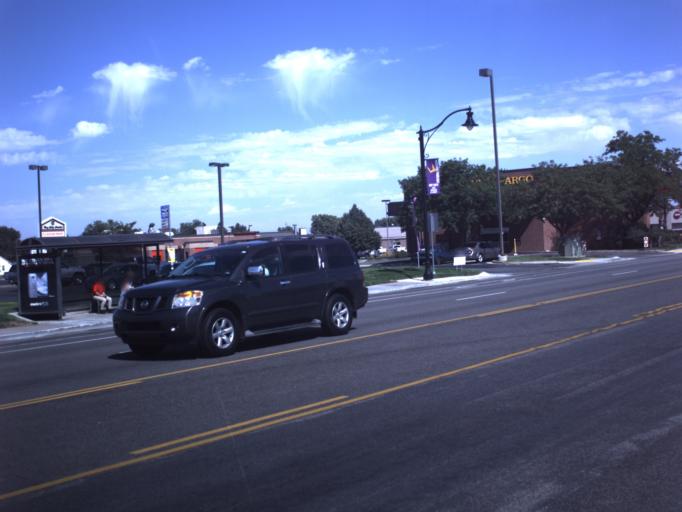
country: US
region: Utah
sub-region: Weber County
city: Roy
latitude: 41.1607
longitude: -112.0259
